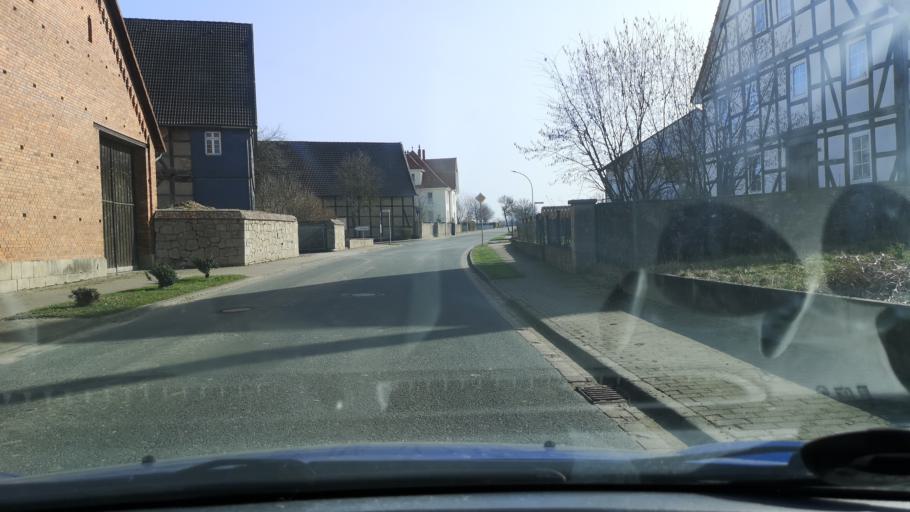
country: DE
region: Lower Saxony
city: Weenzen
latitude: 52.0158
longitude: 9.6236
